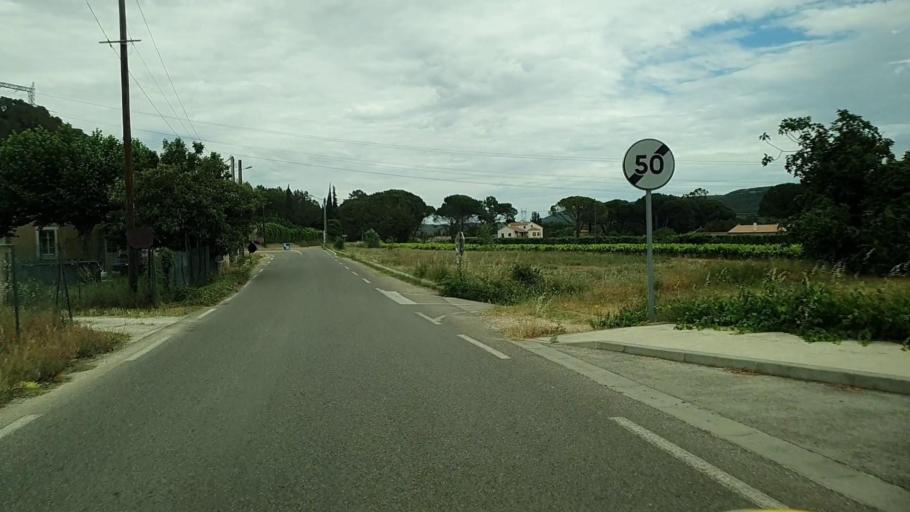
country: FR
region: Languedoc-Roussillon
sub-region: Departement du Gard
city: Tresques
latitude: 44.1164
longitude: 4.5930
